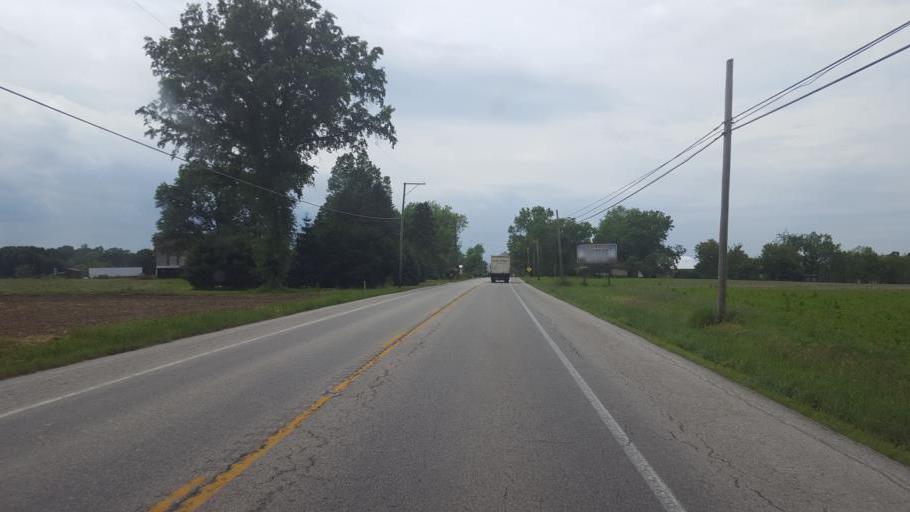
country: US
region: Ohio
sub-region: Wayne County
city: Apple Creek
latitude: 40.7609
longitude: -81.8890
